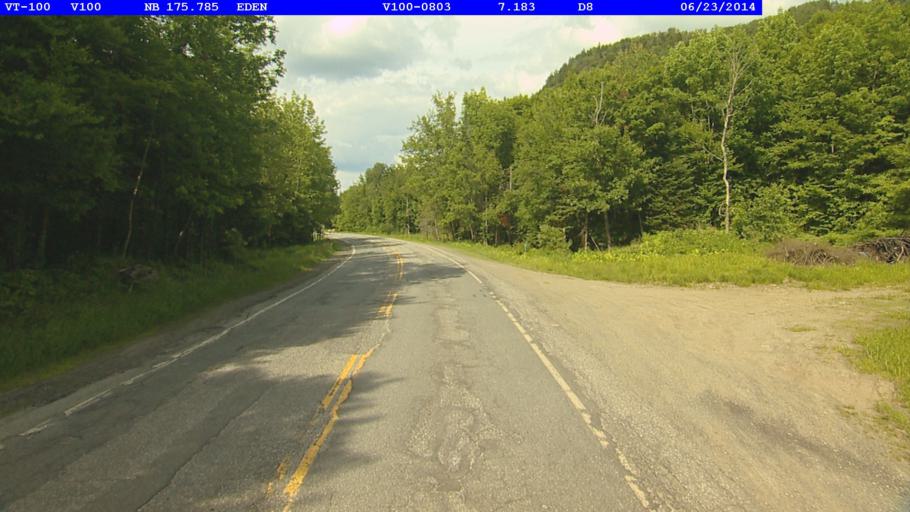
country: US
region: Vermont
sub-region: Lamoille County
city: Hyde Park
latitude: 44.7341
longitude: -72.4716
